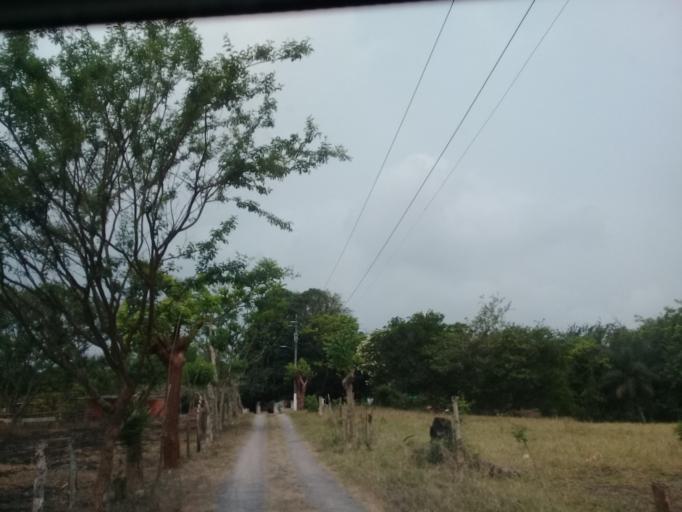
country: MX
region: Veracruz
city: El Tejar
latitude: 19.0609
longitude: -96.1916
